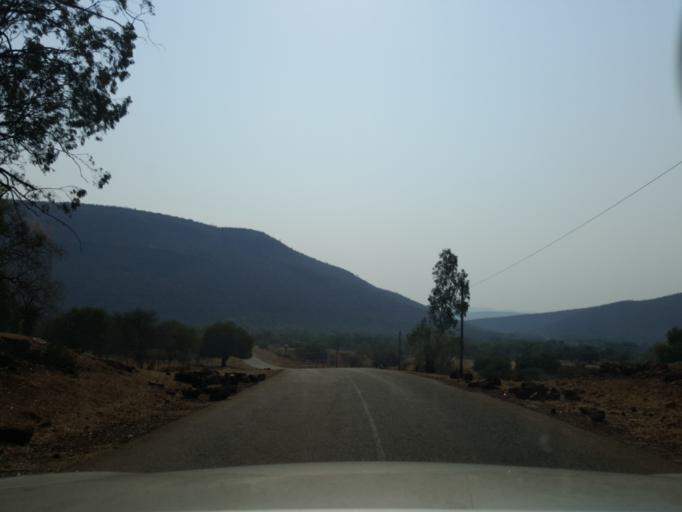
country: BW
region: South East
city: Lobatse
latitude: -25.3295
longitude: 25.7654
